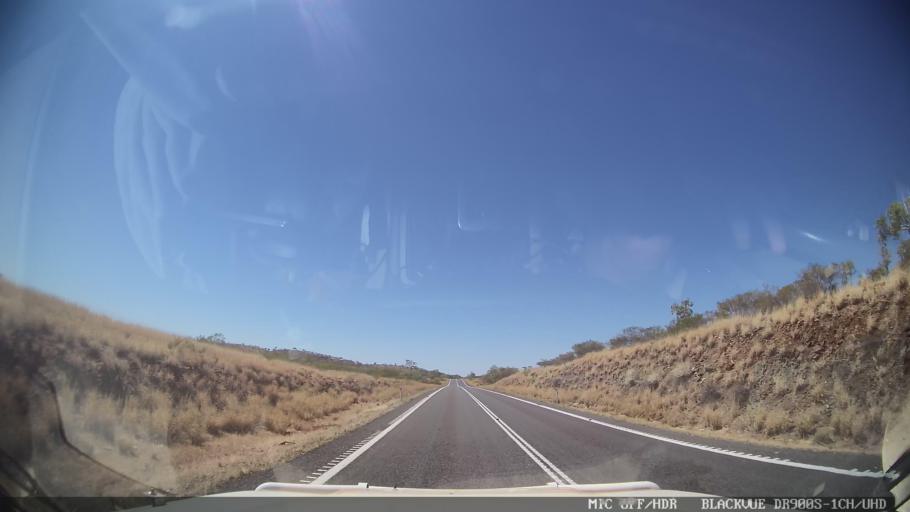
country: AU
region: Queensland
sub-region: Cloncurry
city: Cloncurry
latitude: -20.7171
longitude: 140.4248
